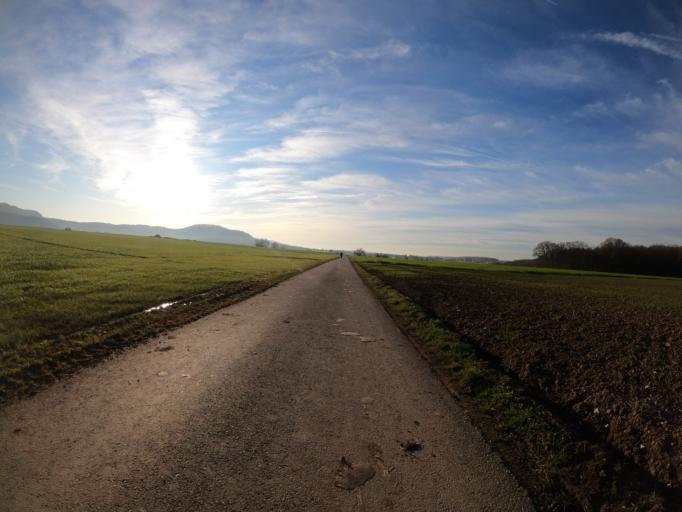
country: DE
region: Baden-Wuerttemberg
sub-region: Regierungsbezirk Stuttgart
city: Boll
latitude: 48.6540
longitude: 9.6034
